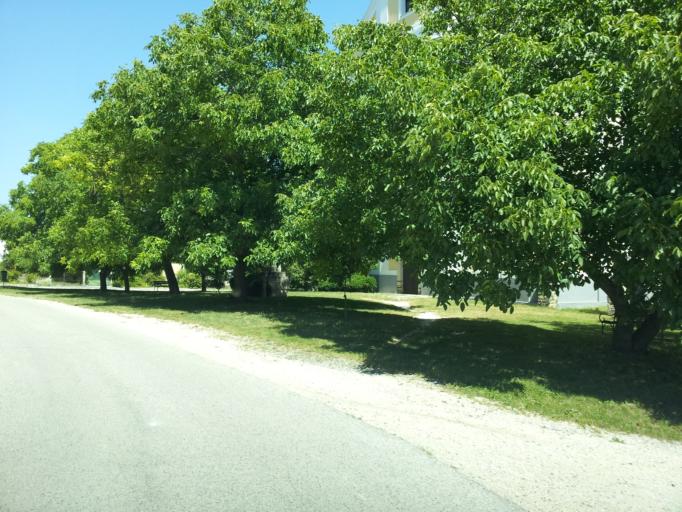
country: HU
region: Veszprem
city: Berhida
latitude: 47.1147
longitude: 18.1344
